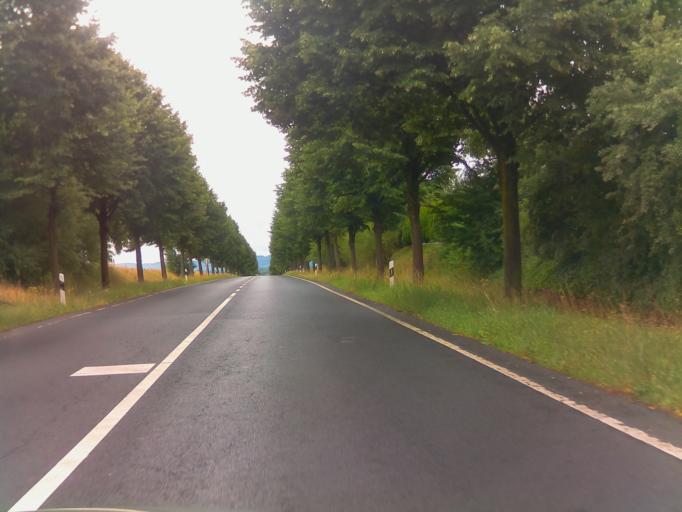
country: LU
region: Grevenmacher
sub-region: Canton de Remich
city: Dalheim
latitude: 49.5318
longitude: 6.2436
